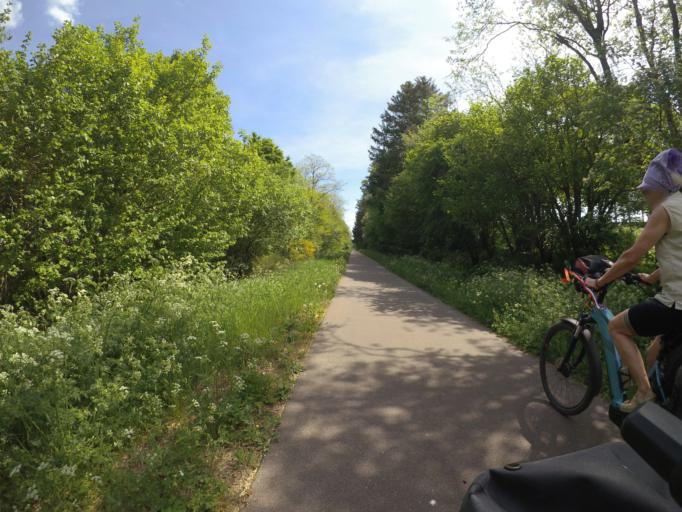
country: BE
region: Wallonia
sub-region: Province de Liege
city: Bullange
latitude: 50.3801
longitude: 6.2932
